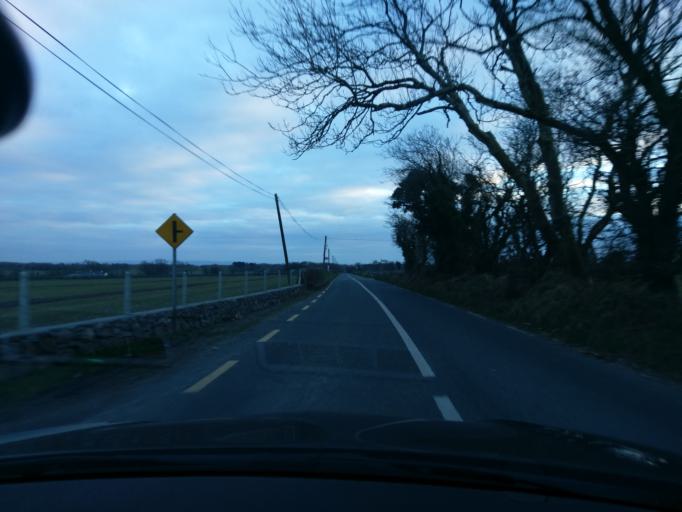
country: IE
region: Connaught
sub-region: County Galway
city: Athenry
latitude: 53.3626
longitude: -8.7754
